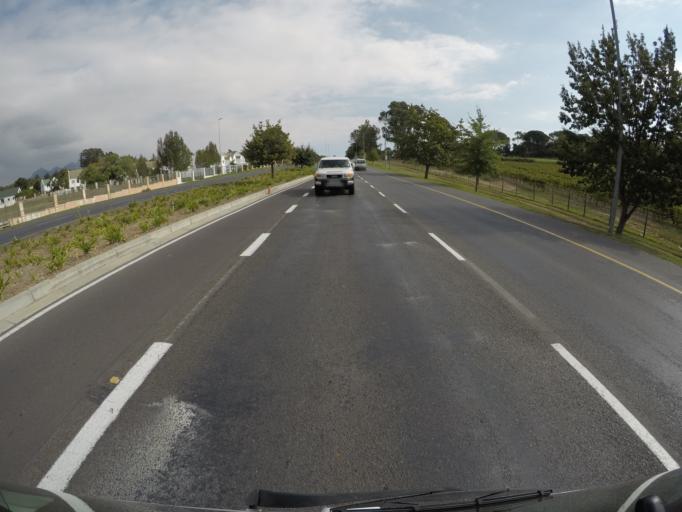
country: ZA
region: Western Cape
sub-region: Cape Winelands District Municipality
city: Stellenbosch
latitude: -33.9577
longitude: 18.8542
